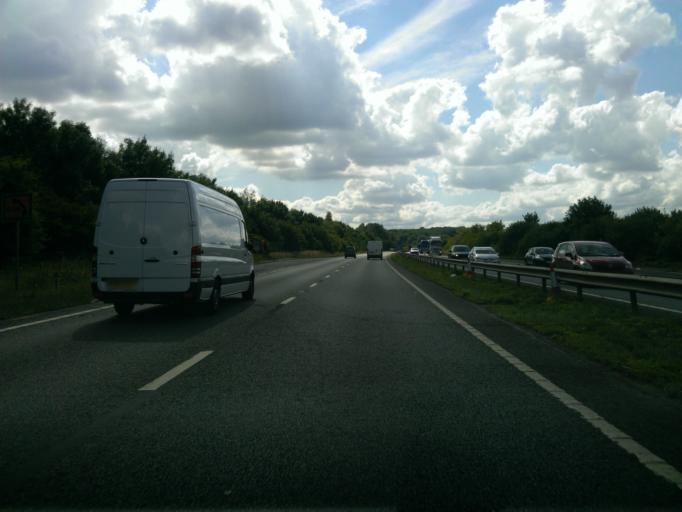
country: GB
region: England
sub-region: Northamptonshire
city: Brixworth
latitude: 52.4024
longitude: -0.9003
